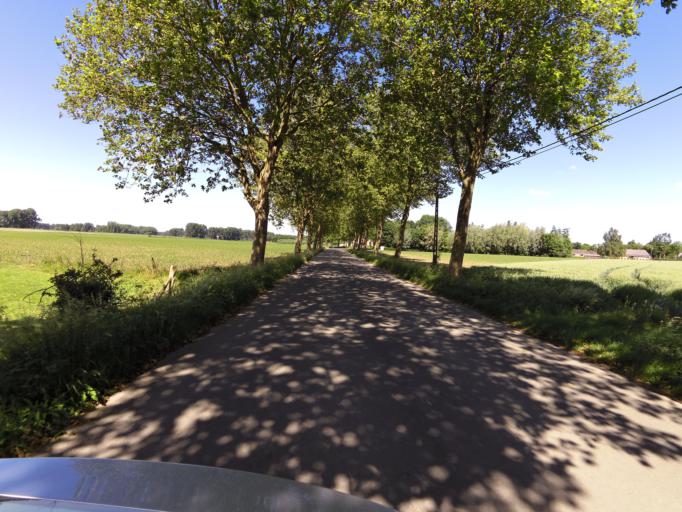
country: BE
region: Flanders
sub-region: Provincie West-Vlaanderen
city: Ieper
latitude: 50.8790
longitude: 2.8274
